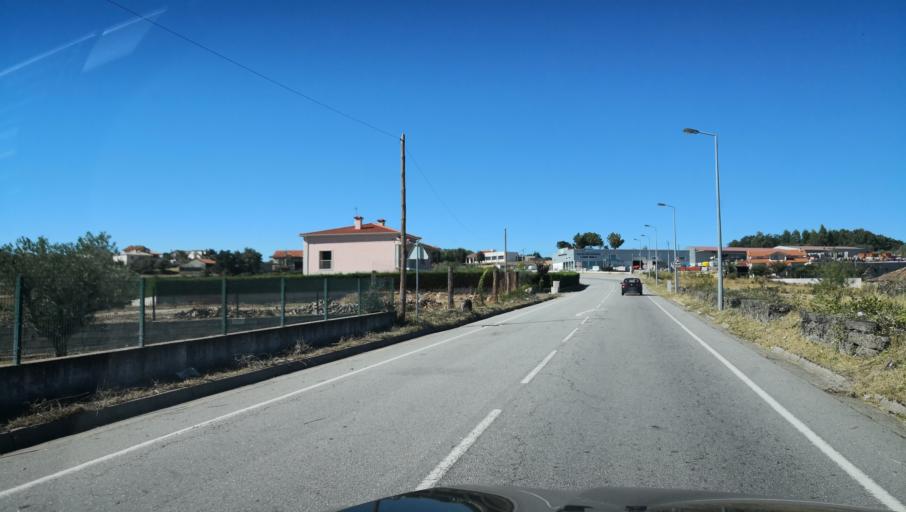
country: PT
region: Vila Real
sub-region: Valpacos
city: Valpacos
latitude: 41.6701
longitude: -7.3380
